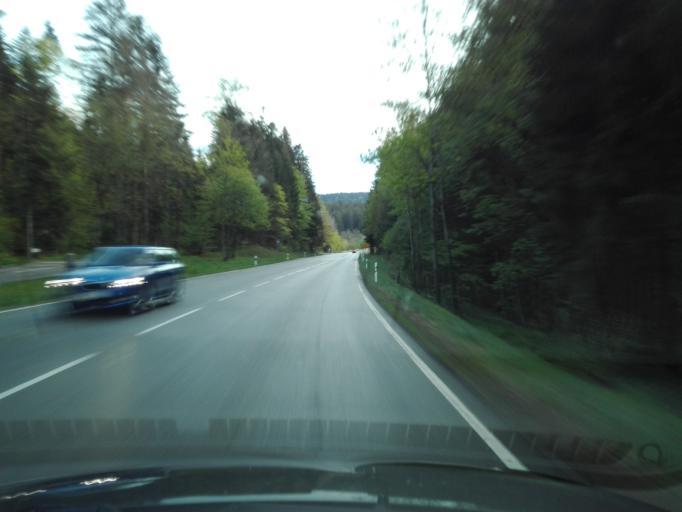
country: DE
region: Bavaria
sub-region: Lower Bavaria
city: Wegscheid
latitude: 48.5749
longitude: 13.7648
